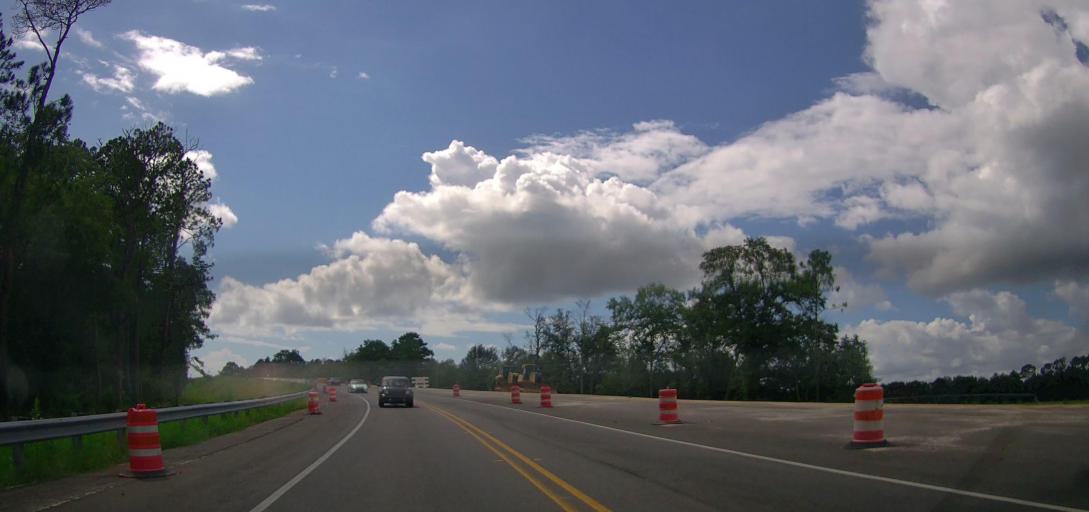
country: US
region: Georgia
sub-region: Coffee County
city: Broxton
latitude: 31.5475
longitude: -82.9376
